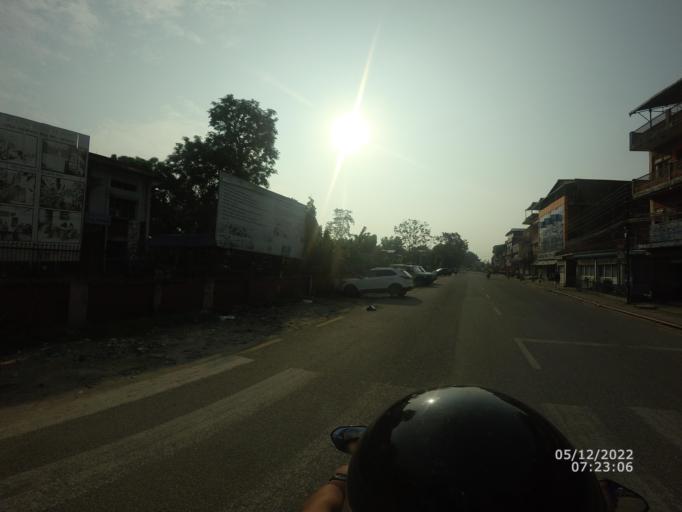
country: NP
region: Central Region
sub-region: Narayani Zone
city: Bharatpur
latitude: 27.6810
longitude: 84.4331
